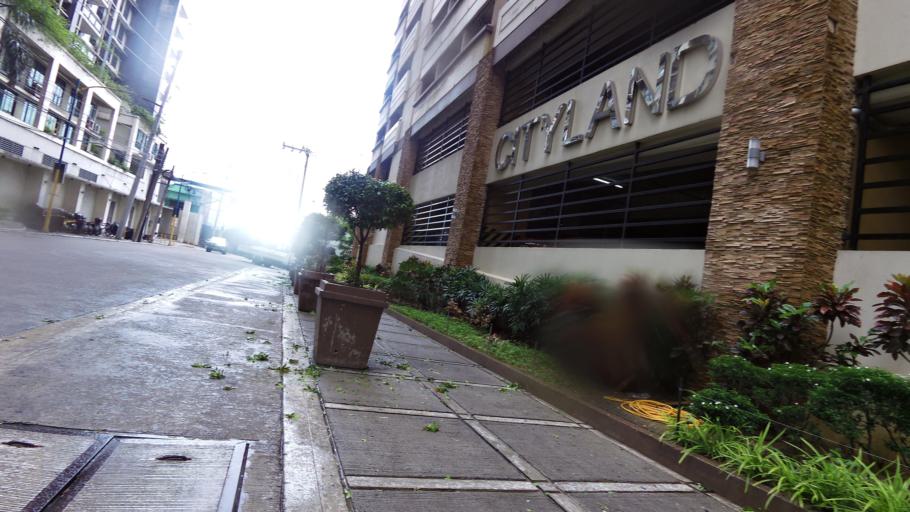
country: PH
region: Metro Manila
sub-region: Mandaluyong
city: Mandaluyong City
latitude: 14.5745
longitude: 121.0506
